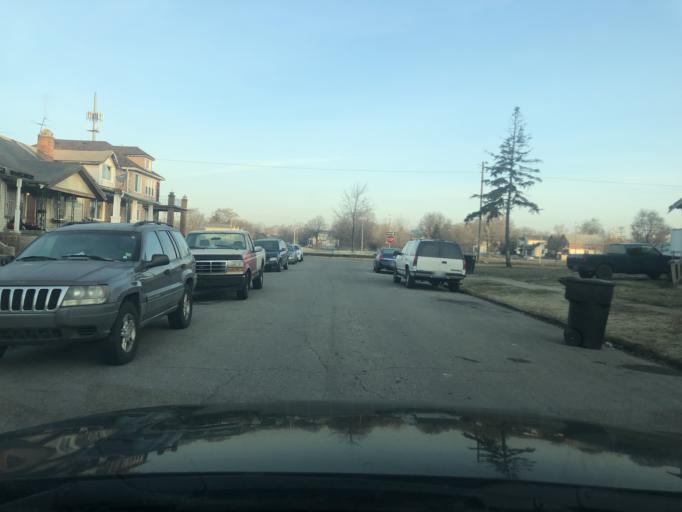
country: US
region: Michigan
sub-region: Wayne County
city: Highland Park
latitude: 42.4040
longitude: -83.1380
